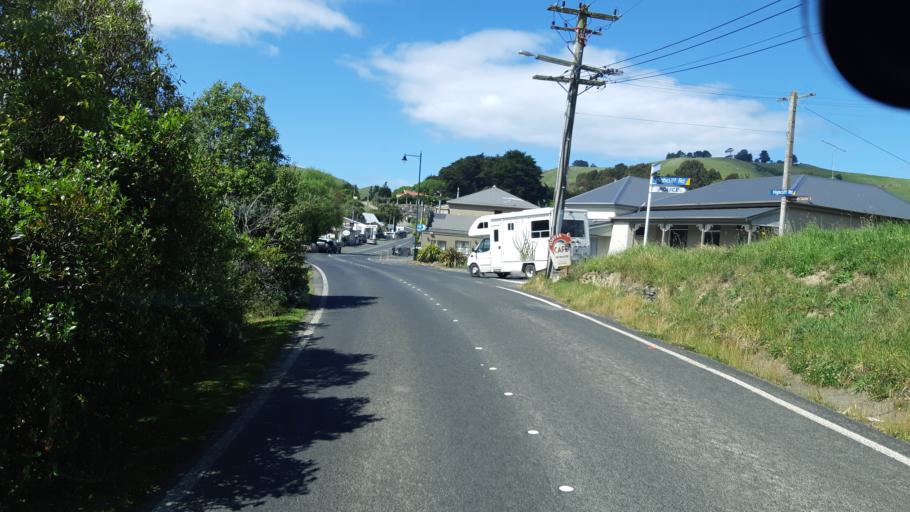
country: NZ
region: Otago
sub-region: Dunedin City
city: Portobello
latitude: -45.8397
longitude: 170.6499
